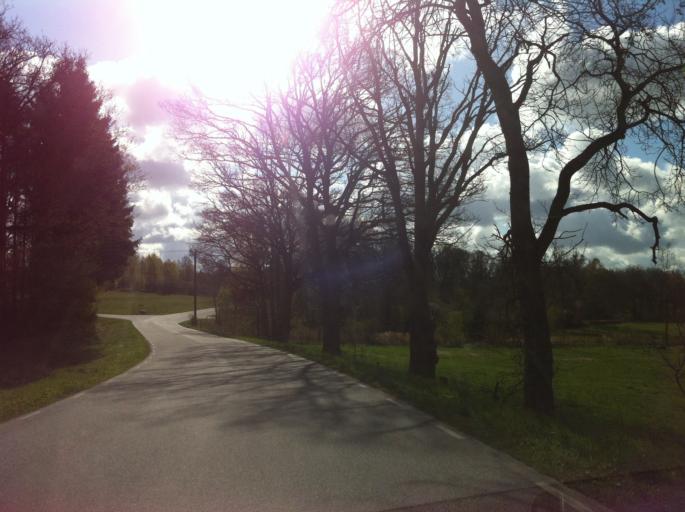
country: SE
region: Skane
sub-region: Hoors Kommun
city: Satofta
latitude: 55.9082
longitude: 13.5769
